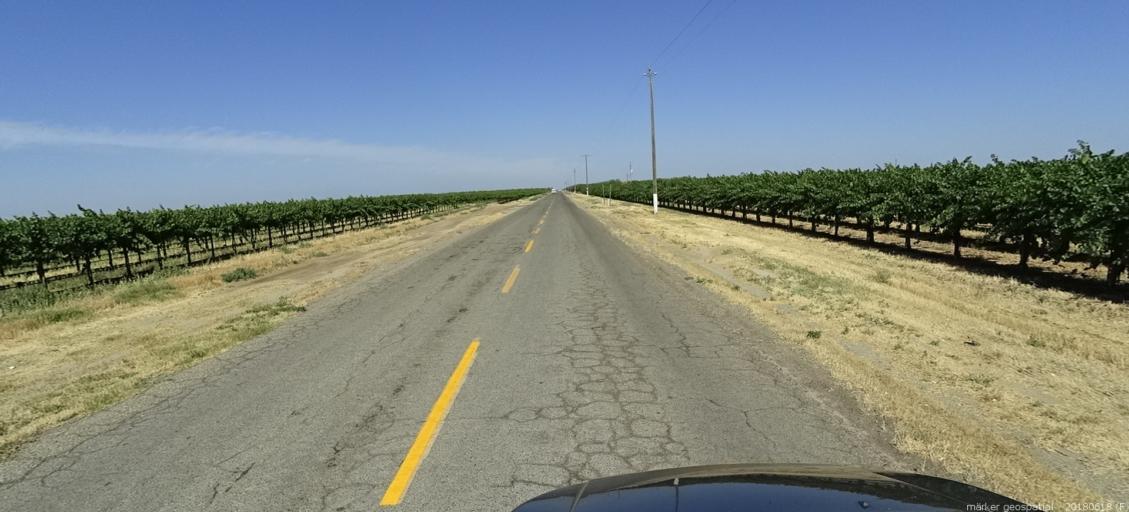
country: US
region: California
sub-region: Fresno County
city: Mendota
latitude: 36.8365
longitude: -120.2163
